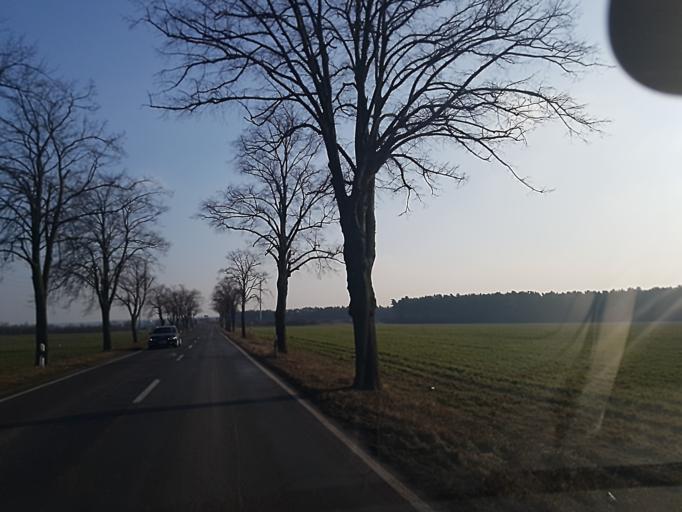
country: DE
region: Brandenburg
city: Wenzlow
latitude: 52.2956
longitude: 12.4577
